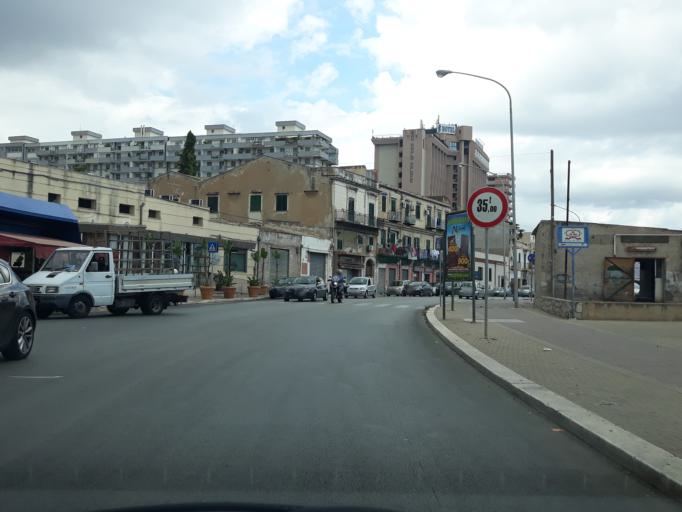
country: IT
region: Sicily
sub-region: Palermo
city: Ciaculli
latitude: 38.1068
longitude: 13.3833
